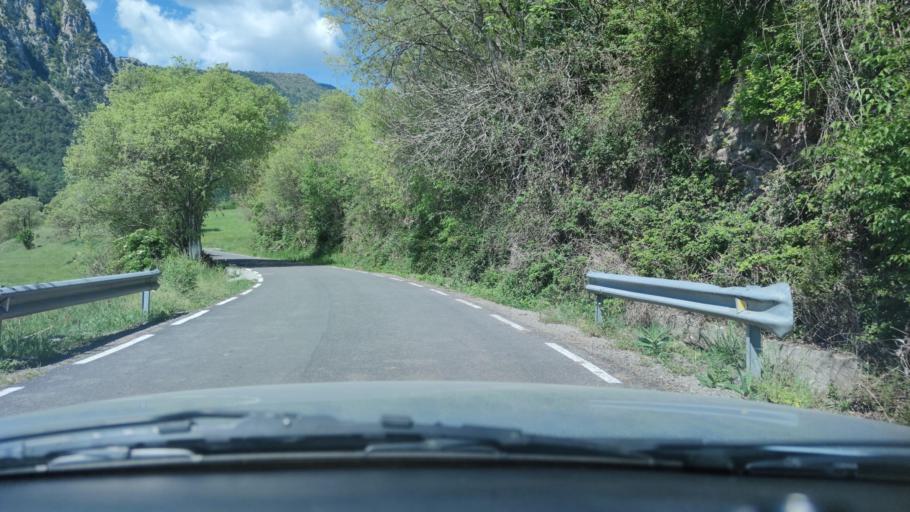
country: ES
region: Catalonia
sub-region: Provincia de Lleida
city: Coll de Nargo
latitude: 42.2931
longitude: 1.3435
